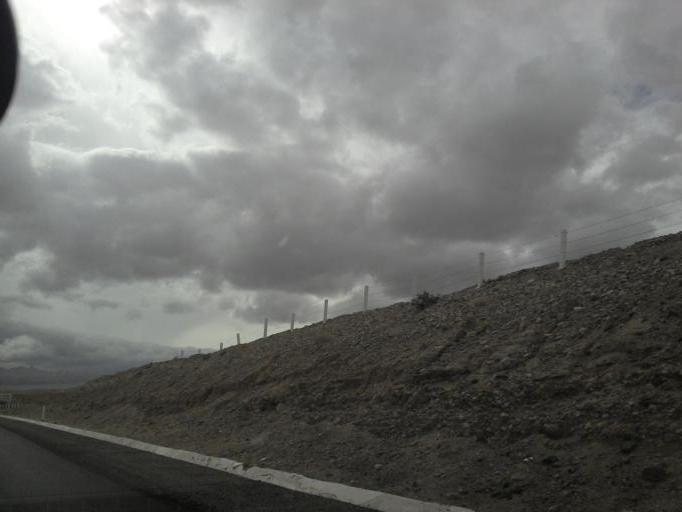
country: MX
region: Baja California
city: Progreso
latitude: 32.5671
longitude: -115.8546
